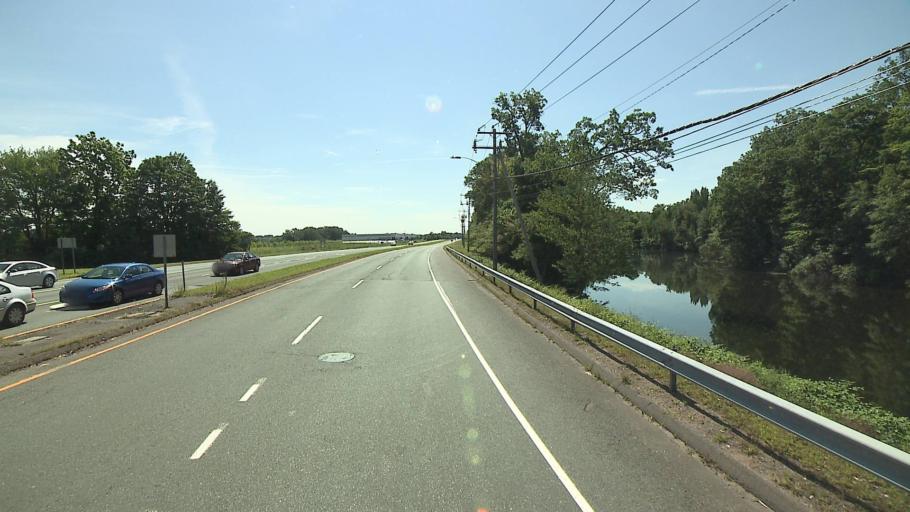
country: US
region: Connecticut
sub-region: Hartford County
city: Tariffville
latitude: 41.8757
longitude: -72.7301
